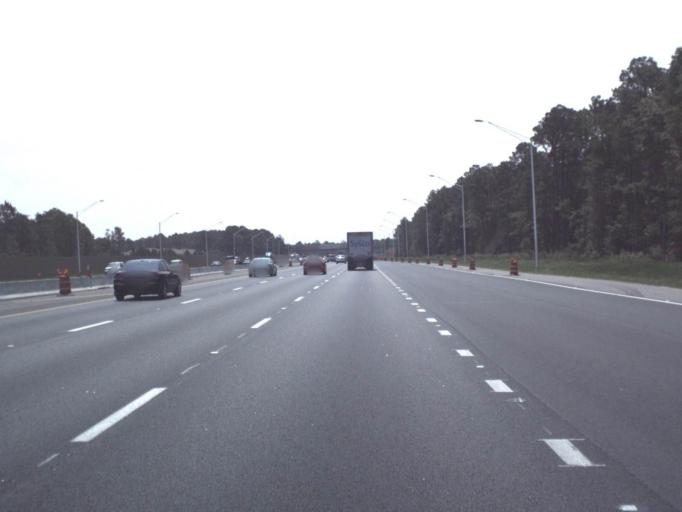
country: US
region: Florida
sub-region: Saint Johns County
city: Fruit Cove
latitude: 30.1076
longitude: -81.5075
